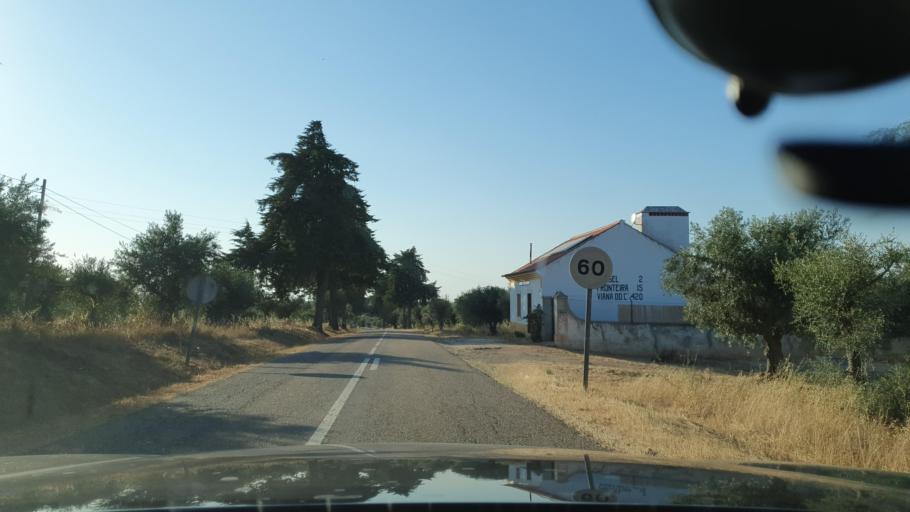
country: PT
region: Portalegre
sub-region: Fronteira
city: Fronteira
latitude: 38.9362
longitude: -7.6693
